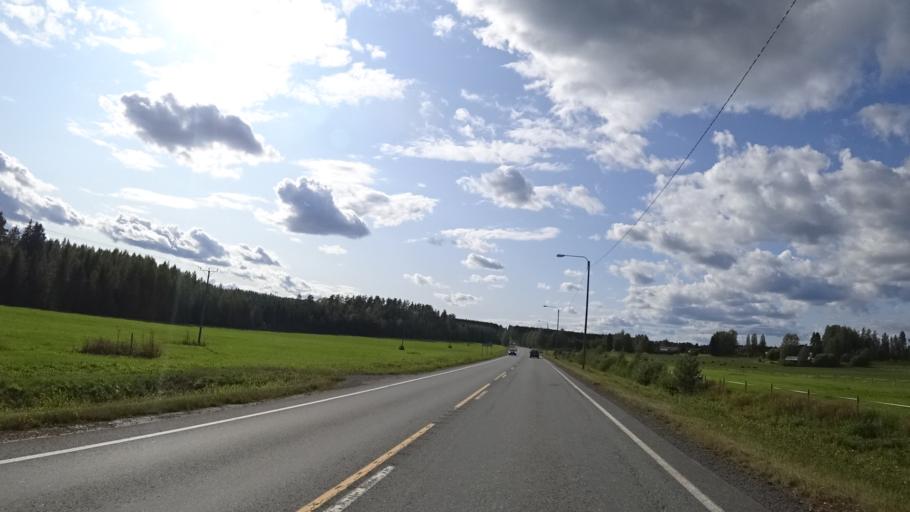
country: FI
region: North Karelia
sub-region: Keski-Karjala
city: Tohmajaervi
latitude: 62.2210
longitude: 30.3910
